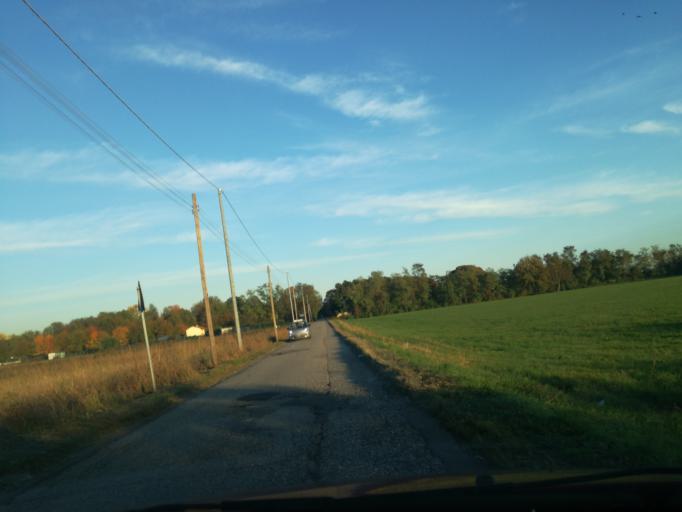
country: IT
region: Lombardy
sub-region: Provincia di Monza e Brianza
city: Burago di Molgora
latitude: 45.6058
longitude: 9.3878
